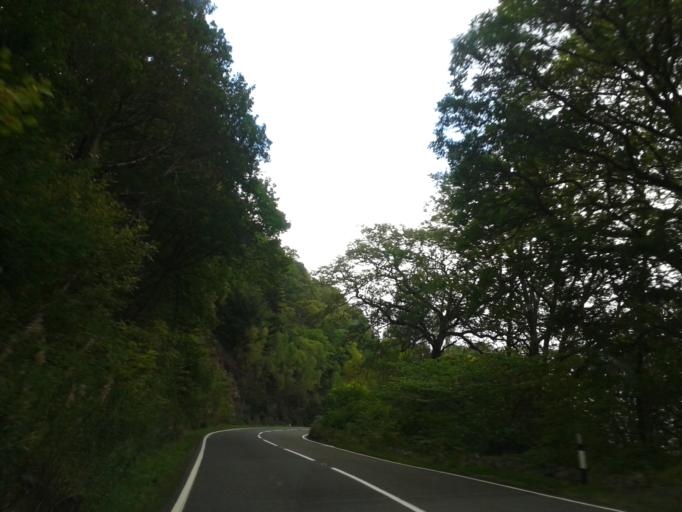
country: GB
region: Scotland
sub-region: Highland
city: Beauly
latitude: 57.2850
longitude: -4.4882
